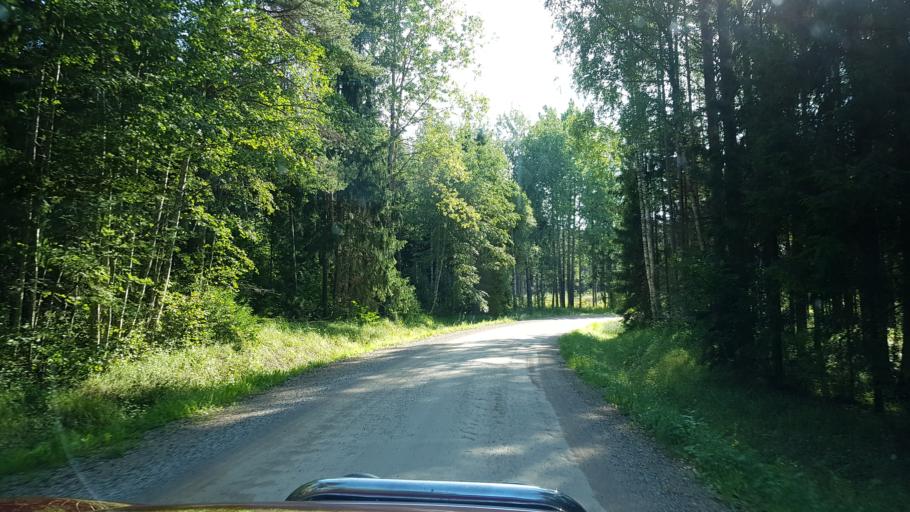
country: LV
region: Apes Novads
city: Ape
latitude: 57.6151
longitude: 26.8164
